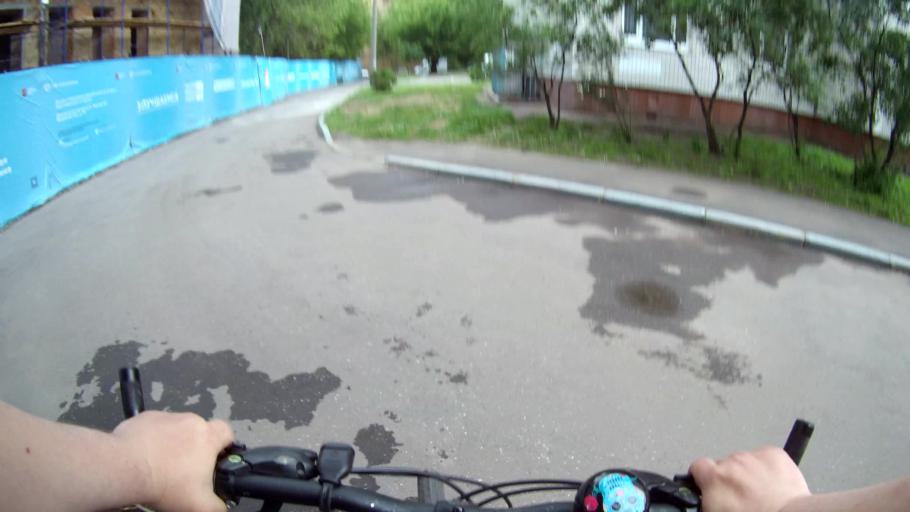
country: RU
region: Moscow
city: Ryazanskiy
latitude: 55.7352
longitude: 37.7504
